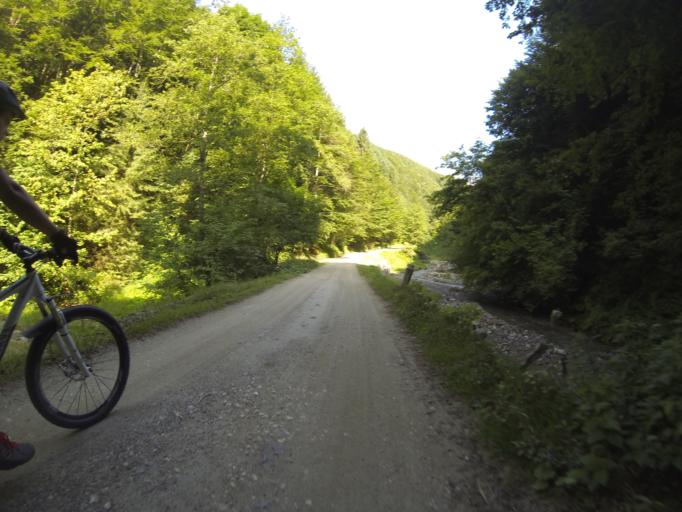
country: RO
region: Valcea
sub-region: Comuna Costesti
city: Bistrita
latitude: 45.2179
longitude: 24.0057
